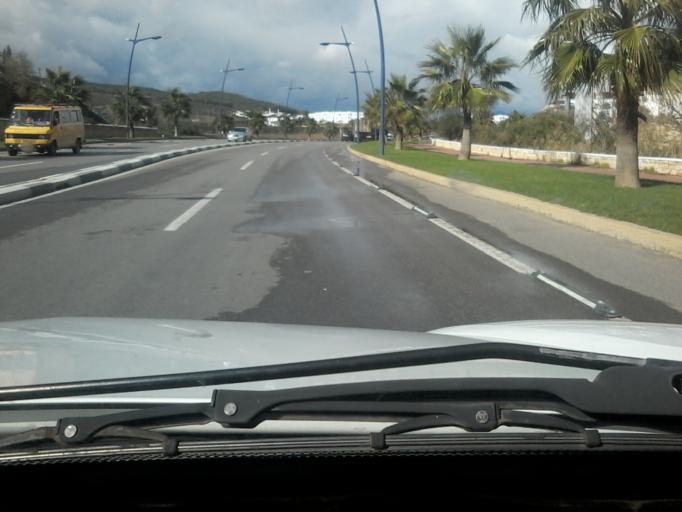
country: MA
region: Tanger-Tetouan
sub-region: Tetouan
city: Martil
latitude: 35.7444
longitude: -5.3449
